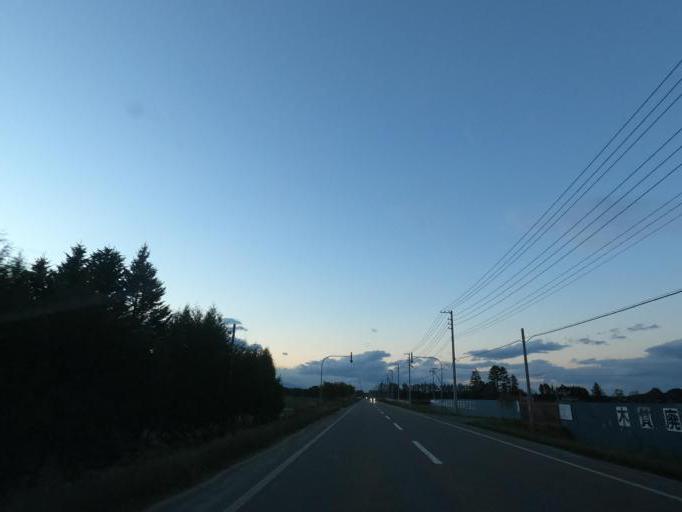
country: JP
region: Hokkaido
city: Obihiro
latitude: 42.6634
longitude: 143.1788
